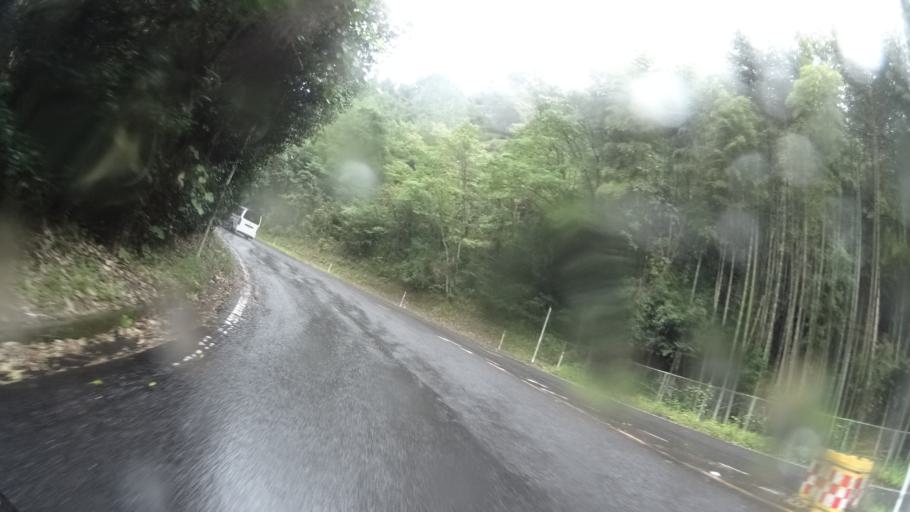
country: JP
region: Kagoshima
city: Kajiki
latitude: 31.8987
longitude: 130.7003
